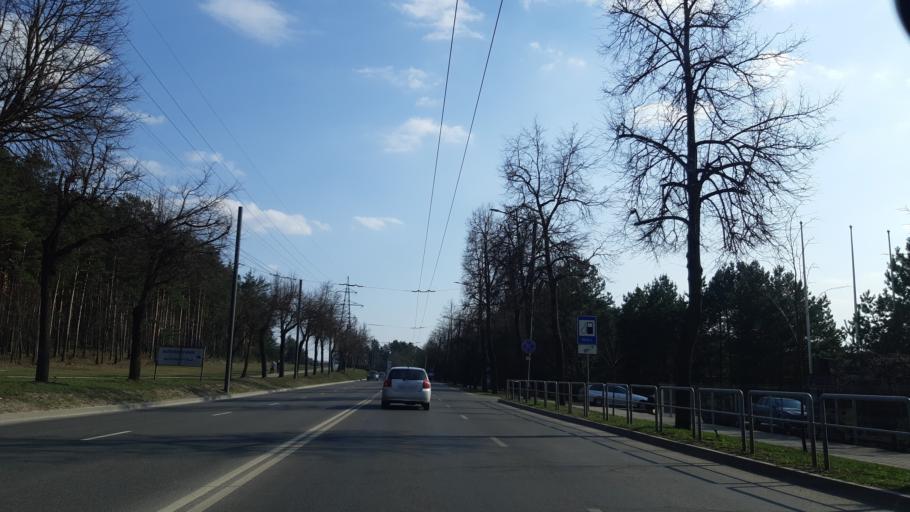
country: LT
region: Kauno apskritis
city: Dainava (Kaunas)
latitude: 54.8842
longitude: 24.0075
